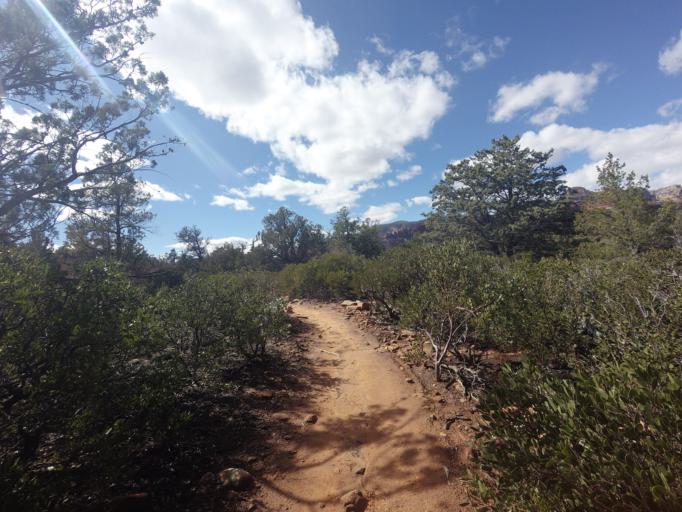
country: US
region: Arizona
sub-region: Yavapai County
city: West Sedona
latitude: 34.8993
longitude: -111.8233
